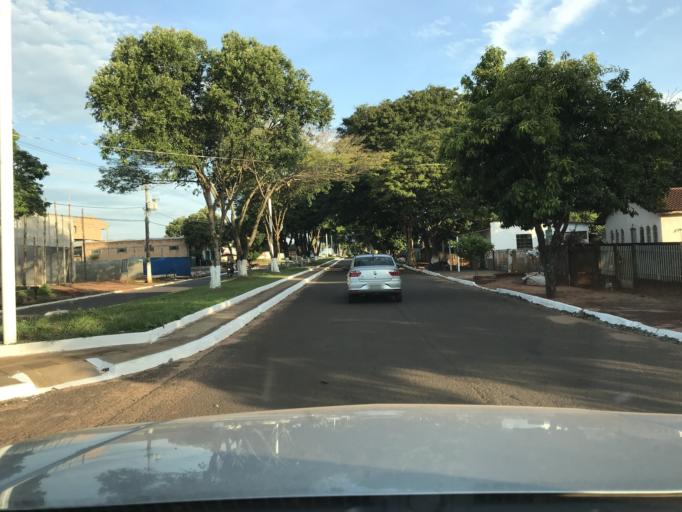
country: BR
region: Mato Grosso do Sul
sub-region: Iguatemi
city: Iguatemi
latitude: -23.6702
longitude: -54.5614
